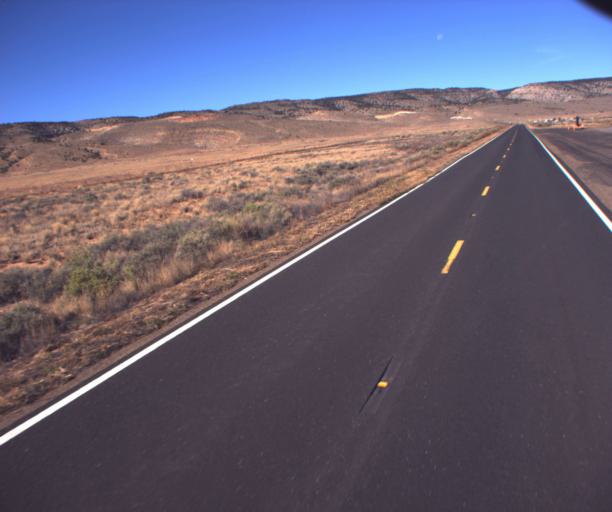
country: US
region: Arizona
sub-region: Coconino County
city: Fredonia
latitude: 36.7287
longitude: -112.0379
